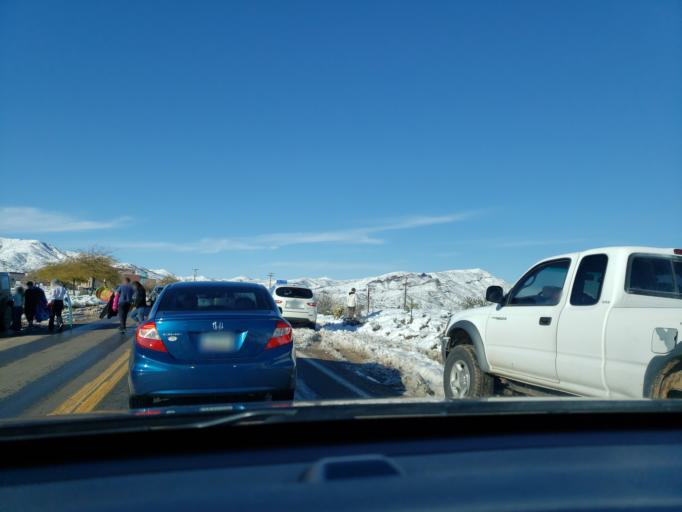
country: US
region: Arizona
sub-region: Maricopa County
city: Carefree
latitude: 33.8653
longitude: -111.8286
